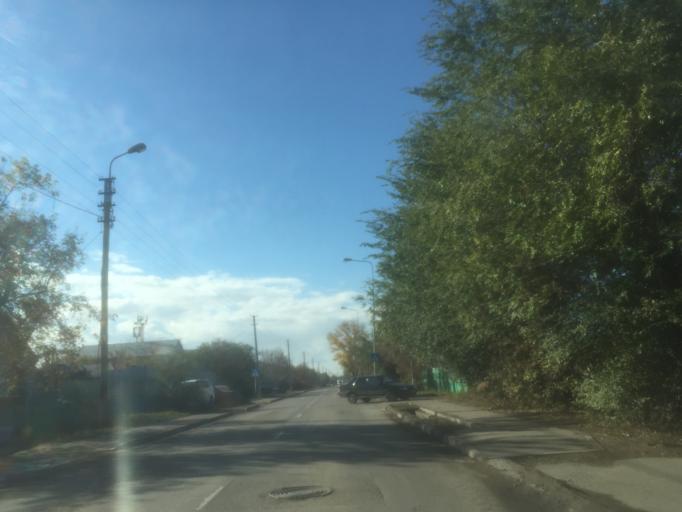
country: KZ
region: Astana Qalasy
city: Astana
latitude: 51.2029
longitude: 71.3725
